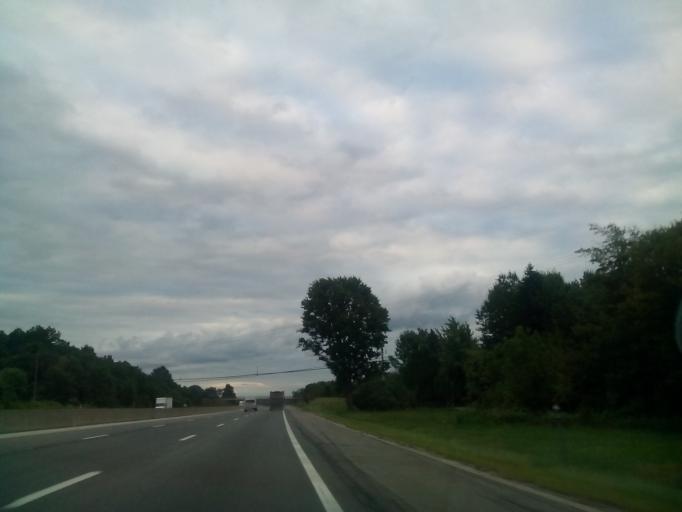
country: US
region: Ohio
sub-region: Trumbull County
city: Newton Falls
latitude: 41.2367
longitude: -80.9814
